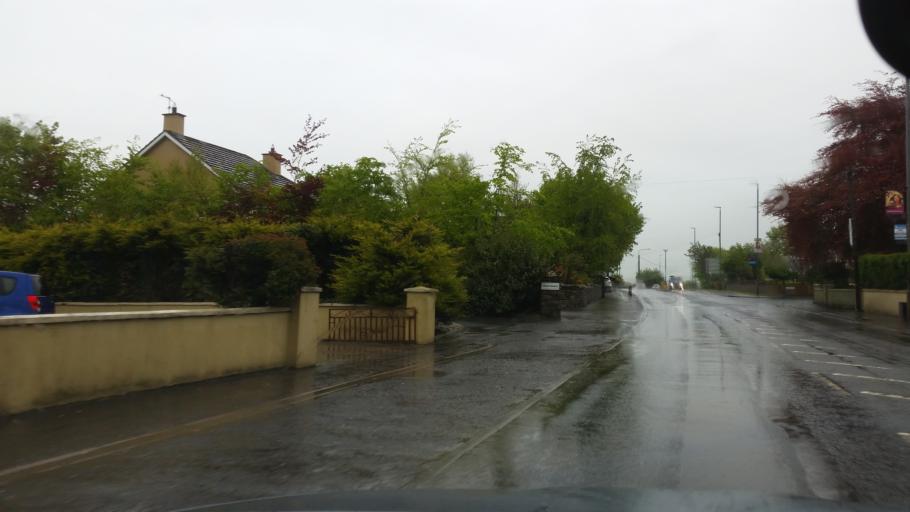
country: GB
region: Northern Ireland
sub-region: Strabane District
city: Strabane
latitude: 54.8401
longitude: -7.4538
